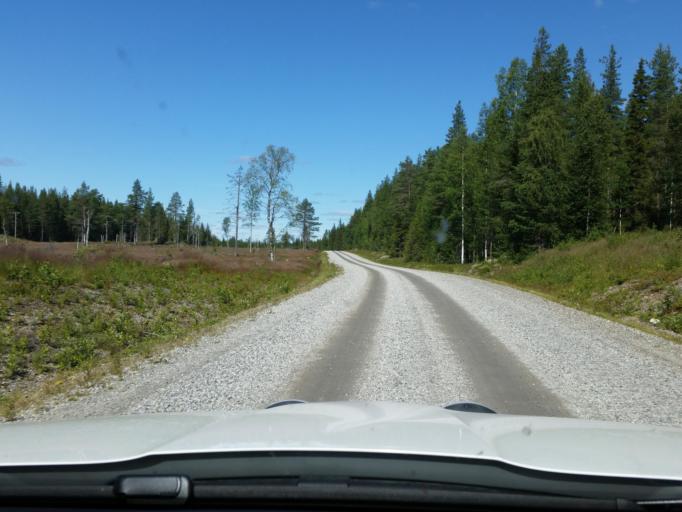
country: SE
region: Vaesterbotten
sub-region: Skelleftea Kommun
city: Storvik
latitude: 65.2608
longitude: 20.6904
